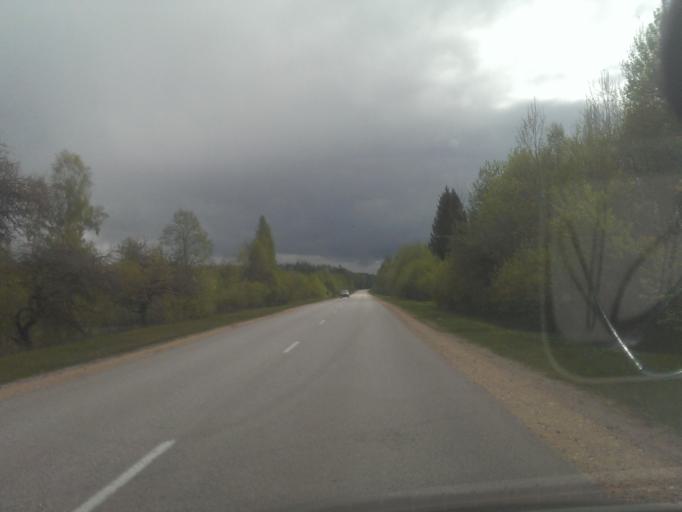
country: LV
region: Ventspils Rajons
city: Piltene
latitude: 57.1702
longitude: 21.6727
